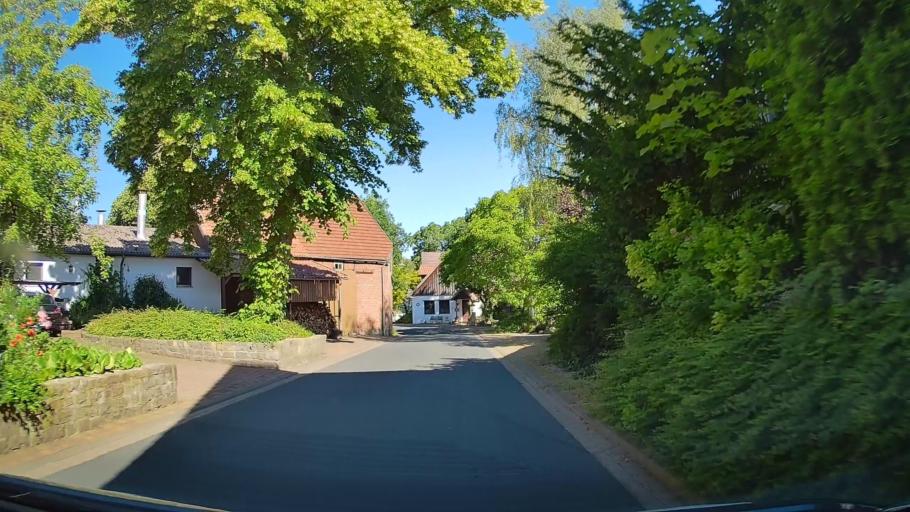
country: DE
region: Lower Saxony
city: Vahlbruch
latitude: 51.9694
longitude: 9.3558
